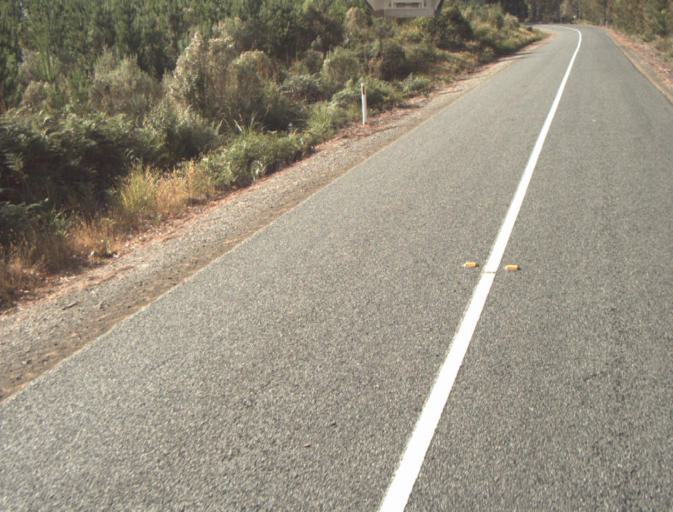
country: AU
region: Tasmania
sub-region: Dorset
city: Bridport
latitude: -41.1439
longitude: 147.2294
